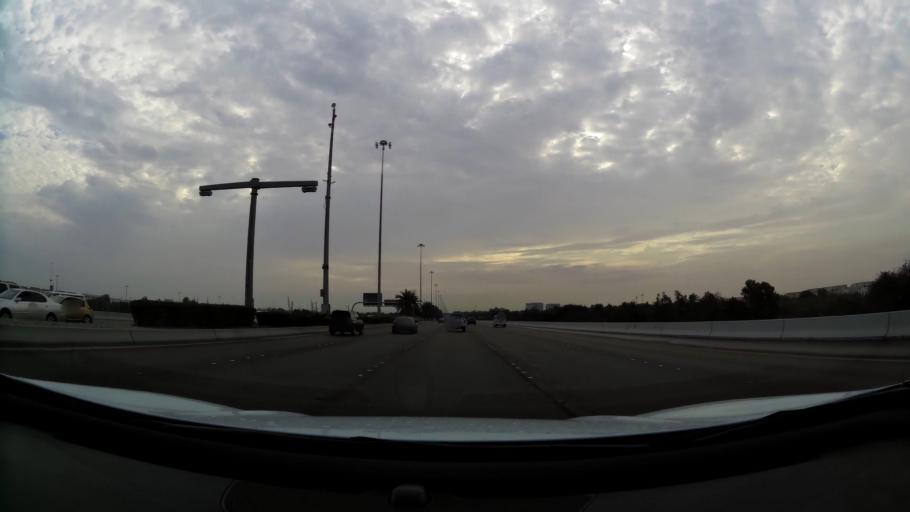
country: AE
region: Abu Dhabi
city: Abu Dhabi
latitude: 24.4023
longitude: 54.4895
